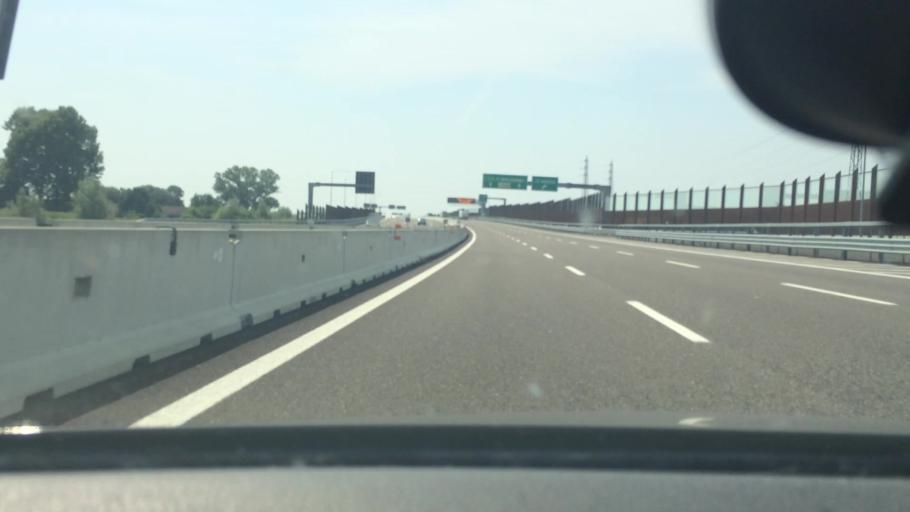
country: IT
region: Lombardy
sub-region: Citta metropolitana di Milano
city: Pozzuolo Martesana
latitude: 45.5118
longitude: 9.4406
